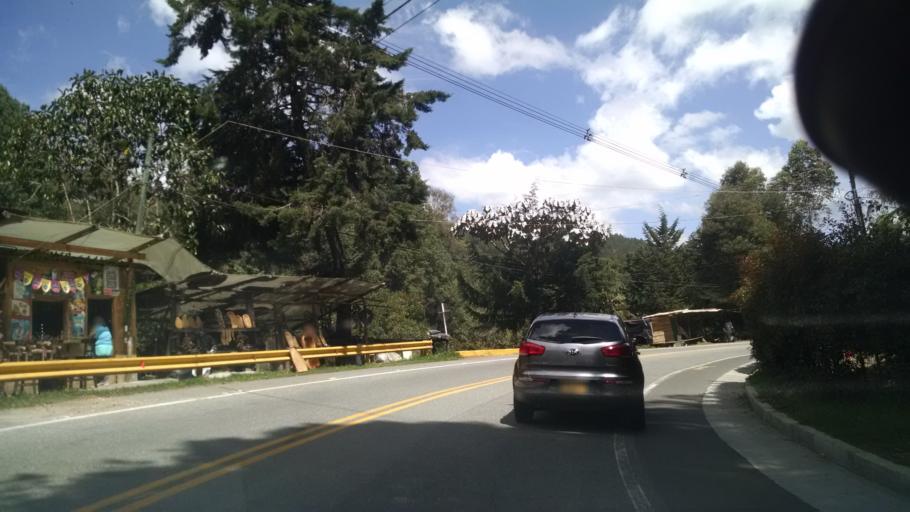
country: CO
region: Antioquia
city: El Retiro
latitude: 6.1304
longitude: -75.5046
